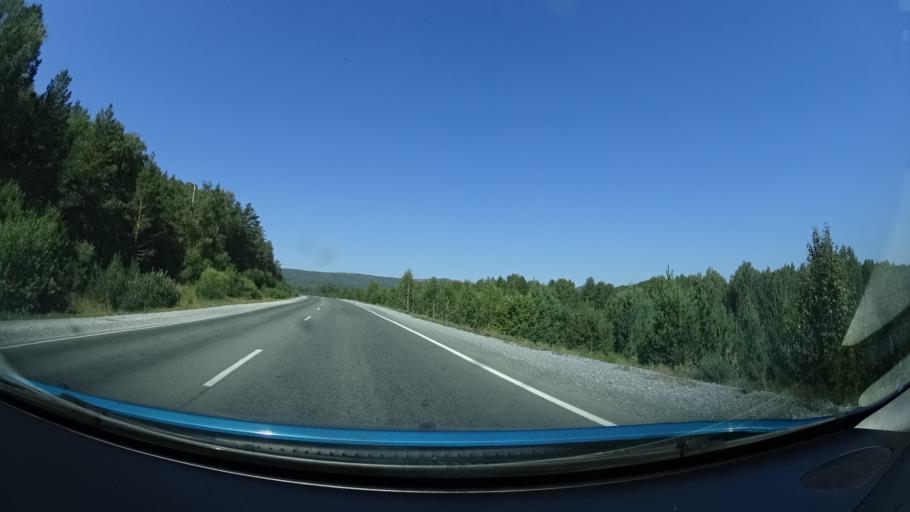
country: RU
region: Bashkortostan
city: Abzakovo
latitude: 53.8552
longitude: 58.5756
